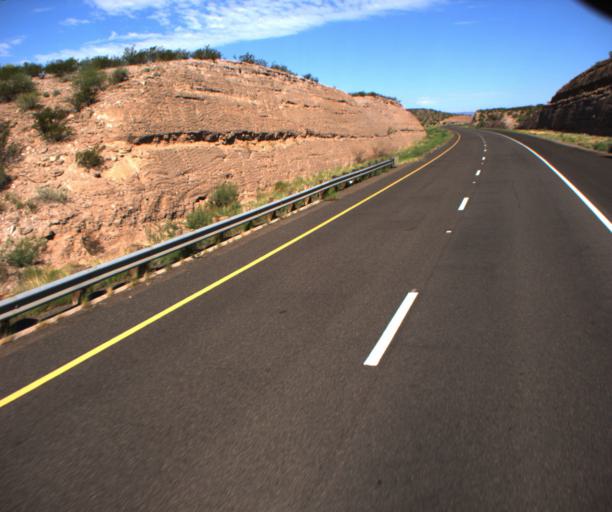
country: US
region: Arizona
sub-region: Greenlee County
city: Clifton
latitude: 32.9726
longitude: -109.2410
